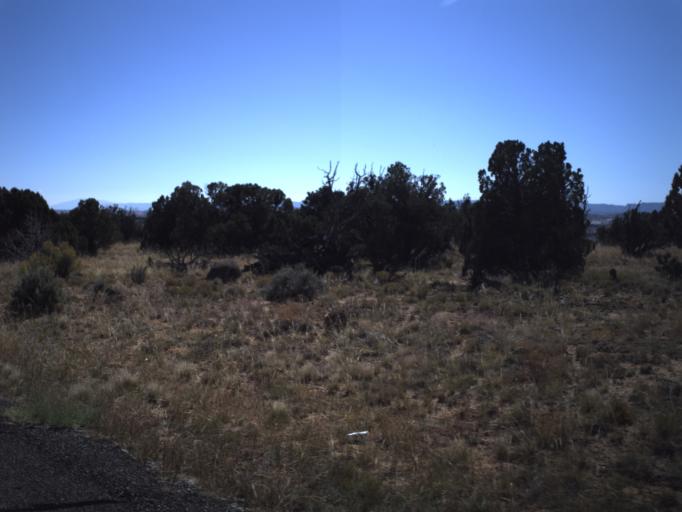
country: US
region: Utah
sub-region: Wayne County
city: Loa
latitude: 37.8440
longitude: -111.4248
